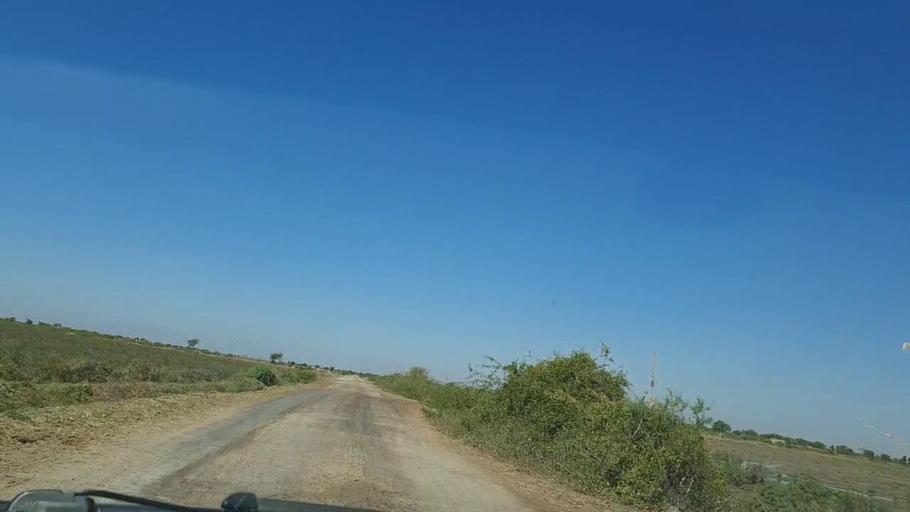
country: PK
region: Sindh
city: Dhoro Naro
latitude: 25.5416
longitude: 69.4997
